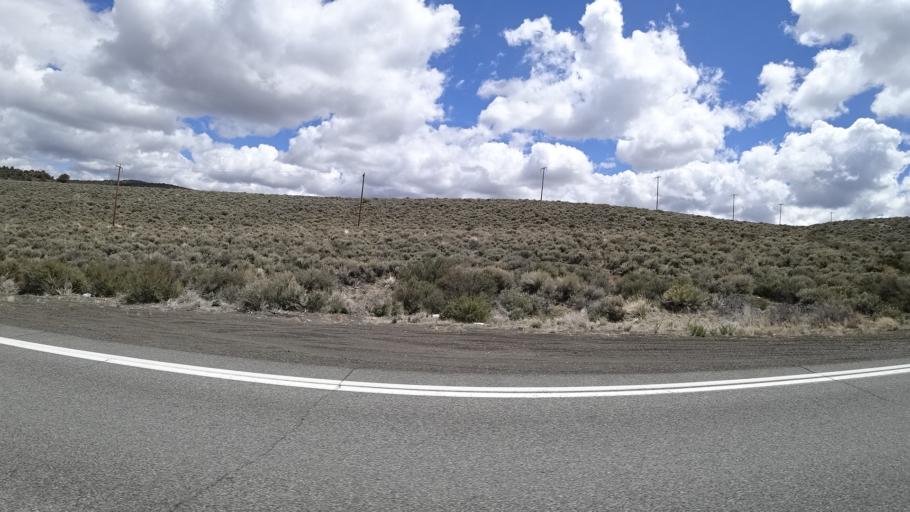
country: US
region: California
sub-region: Mono County
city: Bridgeport
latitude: 38.1727
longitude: -119.1942
